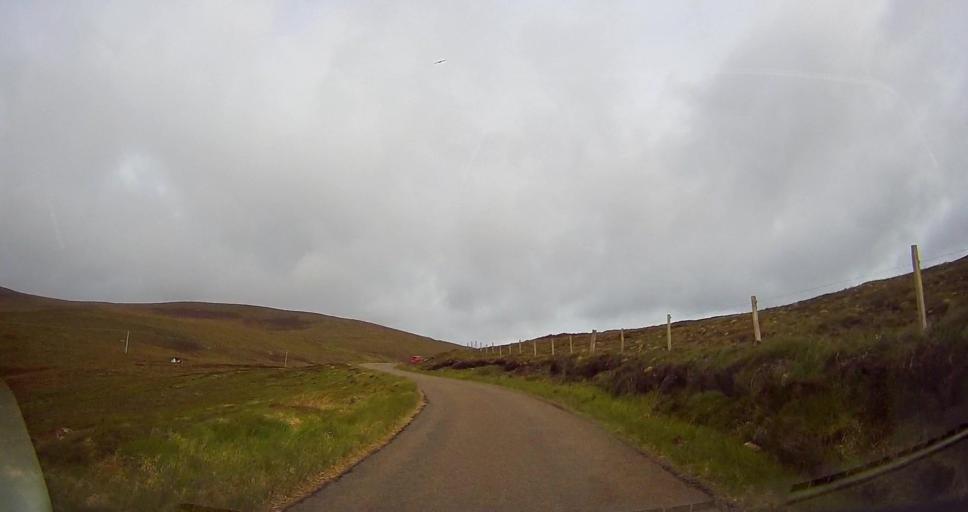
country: GB
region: Scotland
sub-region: Orkney Islands
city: Stromness
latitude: 58.8782
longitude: -3.2474
